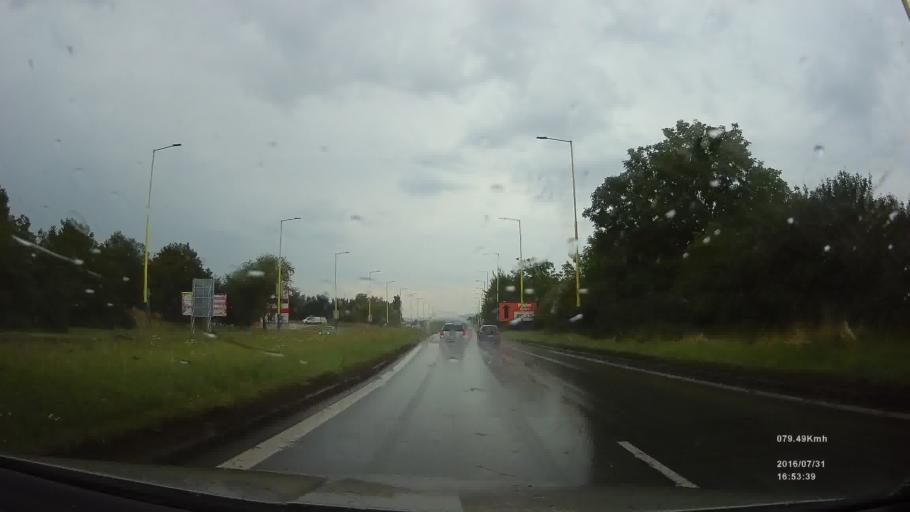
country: SK
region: Presovsky
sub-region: Okres Presov
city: Presov
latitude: 49.0113
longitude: 21.2662
